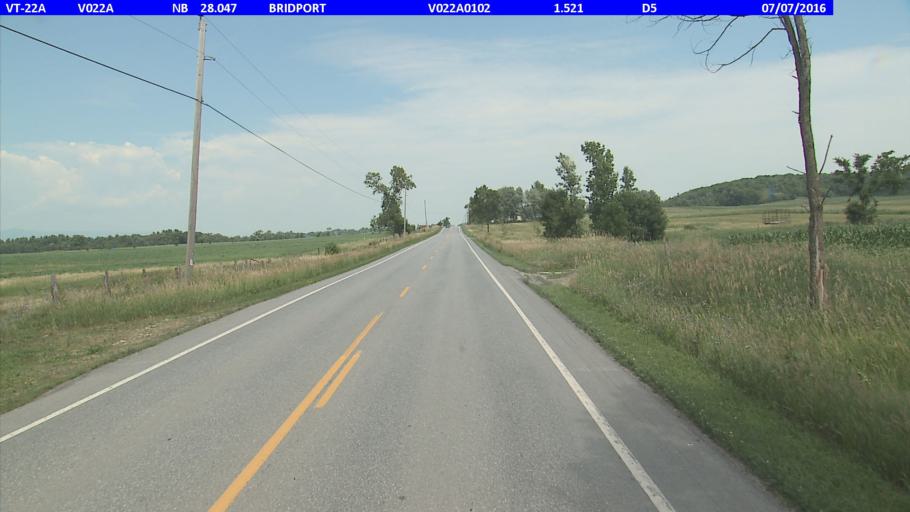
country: US
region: Vermont
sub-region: Addison County
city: Middlebury (village)
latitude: 43.9622
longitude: -73.3088
